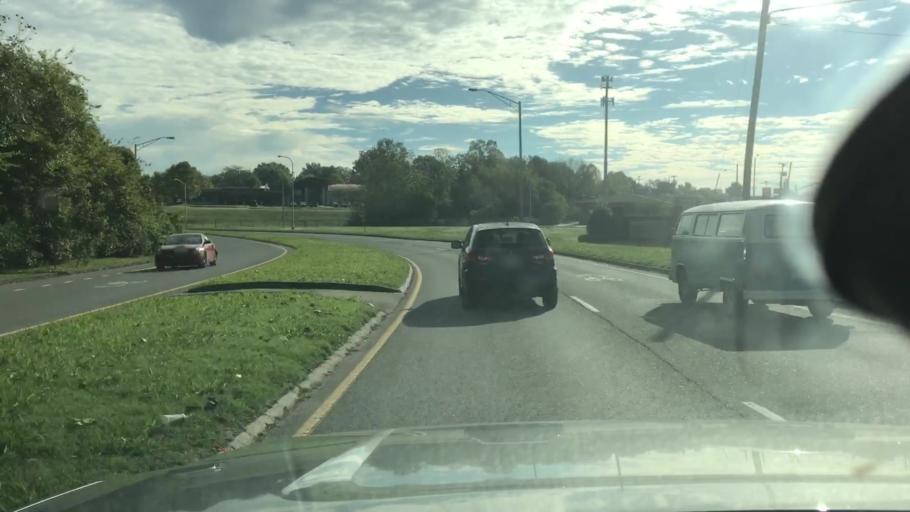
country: US
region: Tennessee
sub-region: Davidson County
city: Nashville
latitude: 36.1888
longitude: -86.8227
